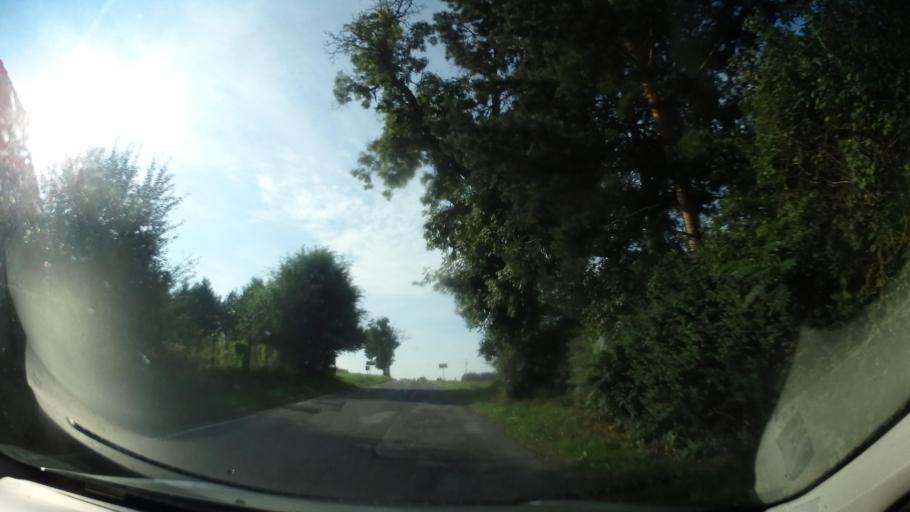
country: CZ
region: Jihocesky
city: Cimelice
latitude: 49.4153
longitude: 14.1187
